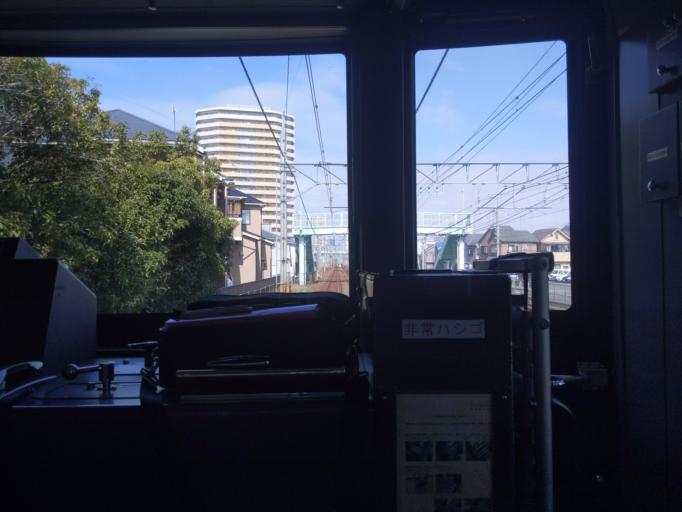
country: JP
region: Saitama
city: Soka
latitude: 35.7841
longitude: 139.7868
